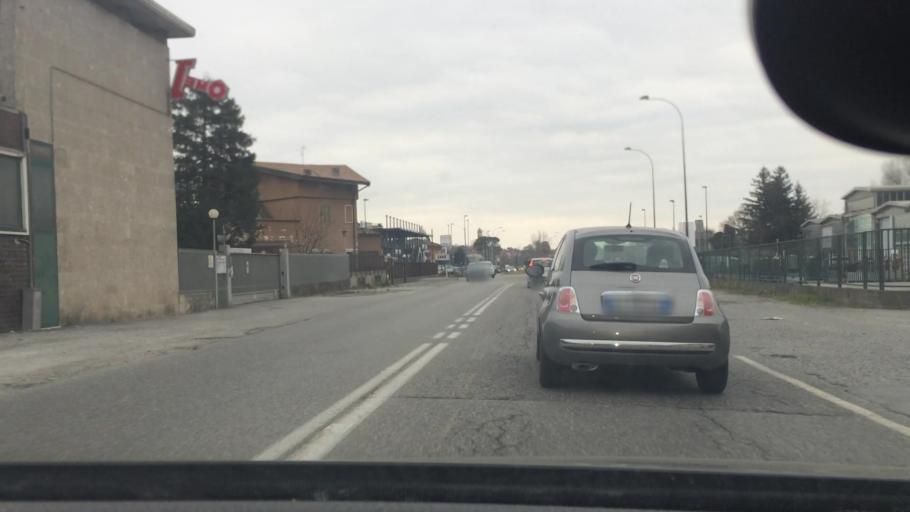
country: IT
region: Lombardy
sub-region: Provincia di Como
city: Merone
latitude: 45.7965
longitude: 9.2406
